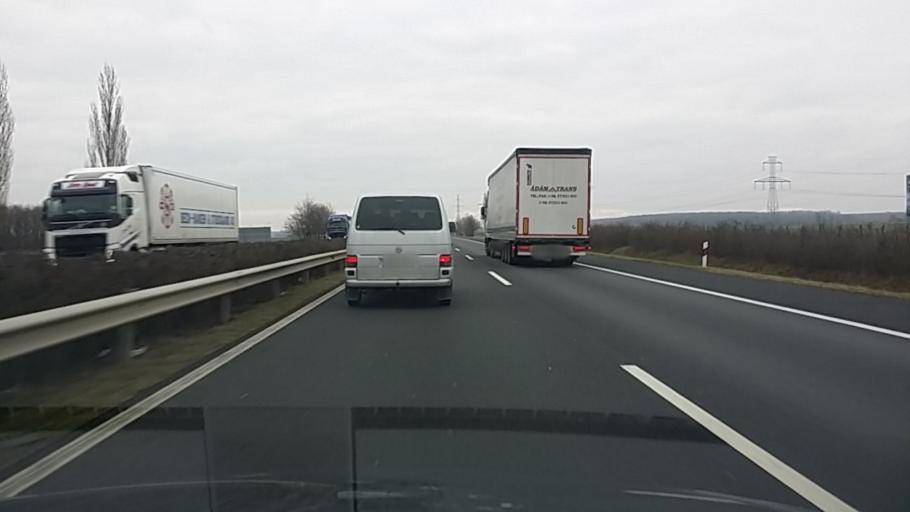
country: HU
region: Gyor-Moson-Sopron
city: Mosonmagyarovar
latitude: 47.8269
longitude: 17.2799
